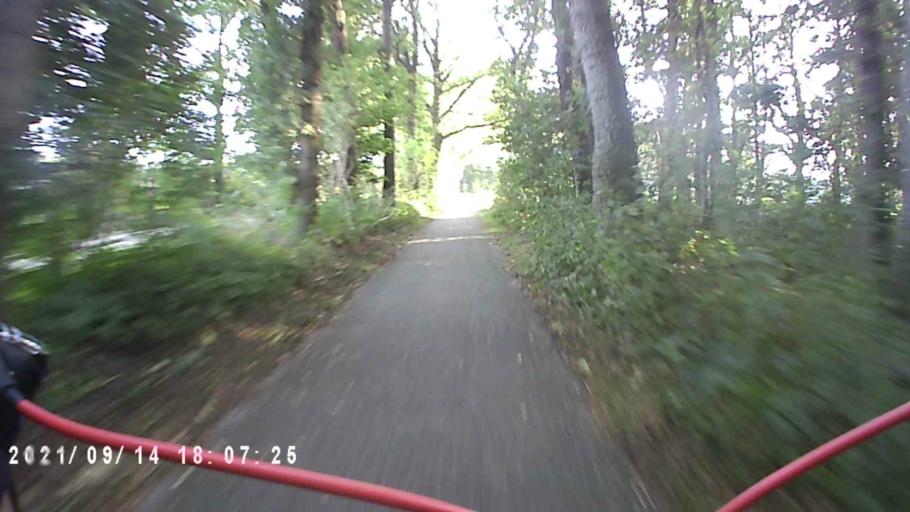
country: NL
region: Drenthe
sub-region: Gemeente Tynaarlo
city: Zuidlaren
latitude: 53.1043
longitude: 6.6563
